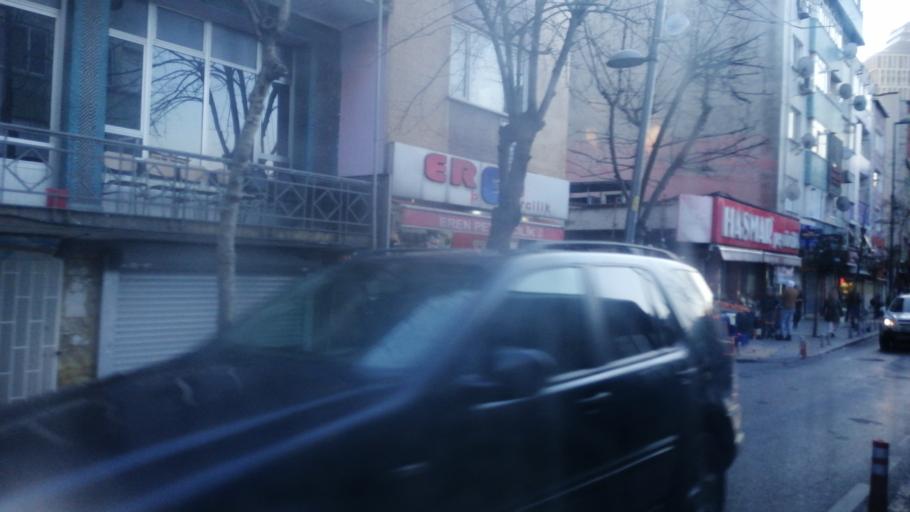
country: TR
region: Istanbul
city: Sisli
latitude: 41.0805
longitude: 28.9935
